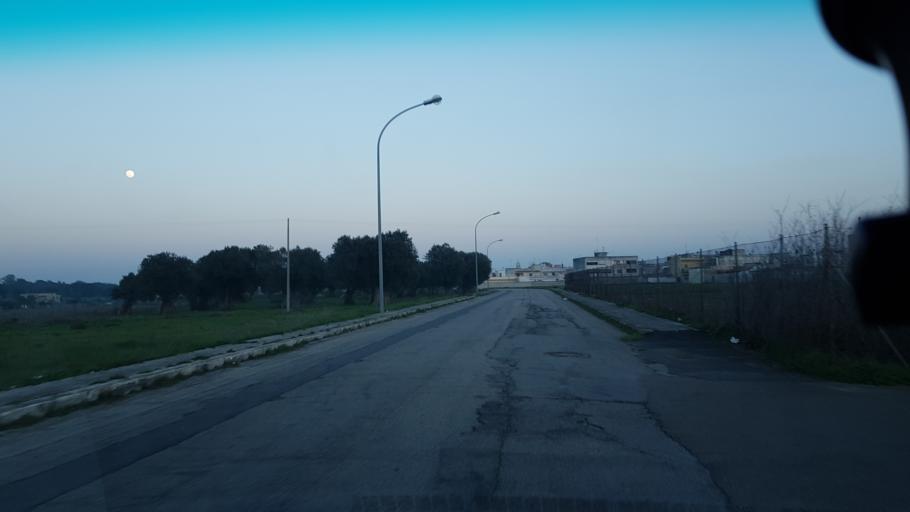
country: IT
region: Apulia
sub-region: Provincia di Brindisi
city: Mesagne
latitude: 40.5642
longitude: 17.7926
